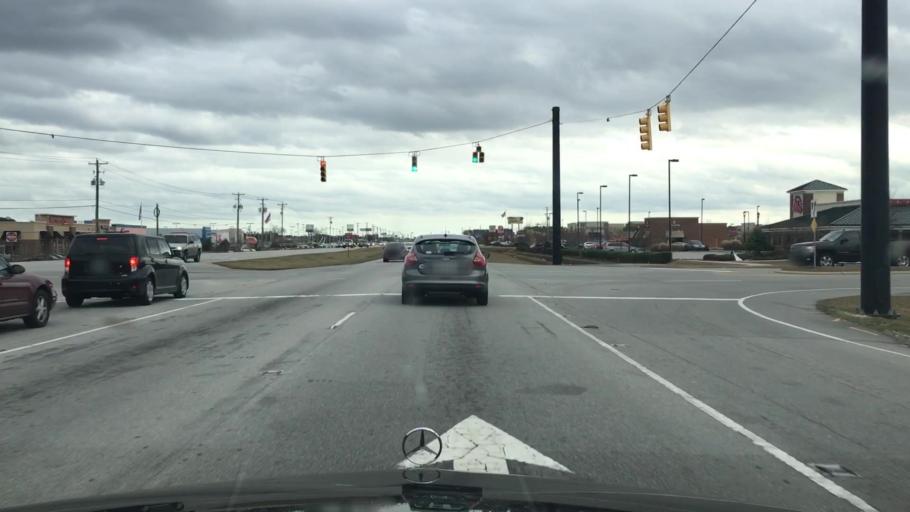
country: US
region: North Carolina
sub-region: Onslow County
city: Pumpkin Center
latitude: 34.7914
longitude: -77.4063
